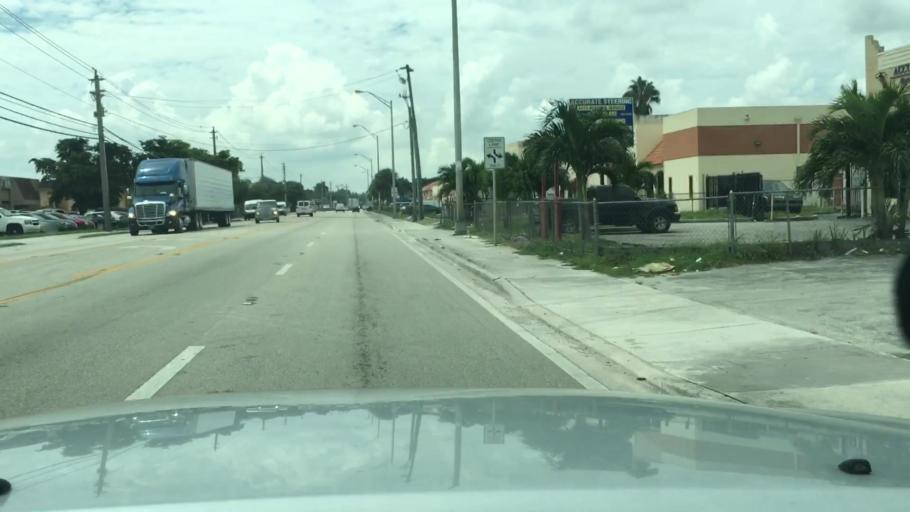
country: US
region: Florida
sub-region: Miami-Dade County
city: Opa-locka
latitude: 25.8966
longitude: -80.2627
